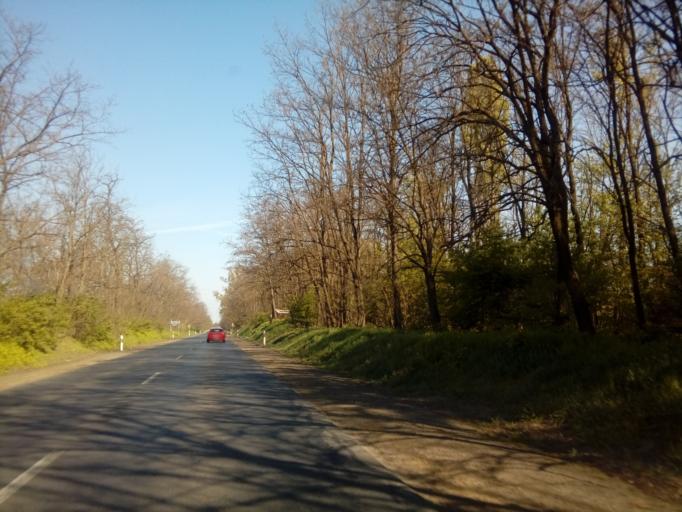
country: HU
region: Szabolcs-Szatmar-Bereg
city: Nyiregyhaza
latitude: 47.9168
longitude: 21.7719
